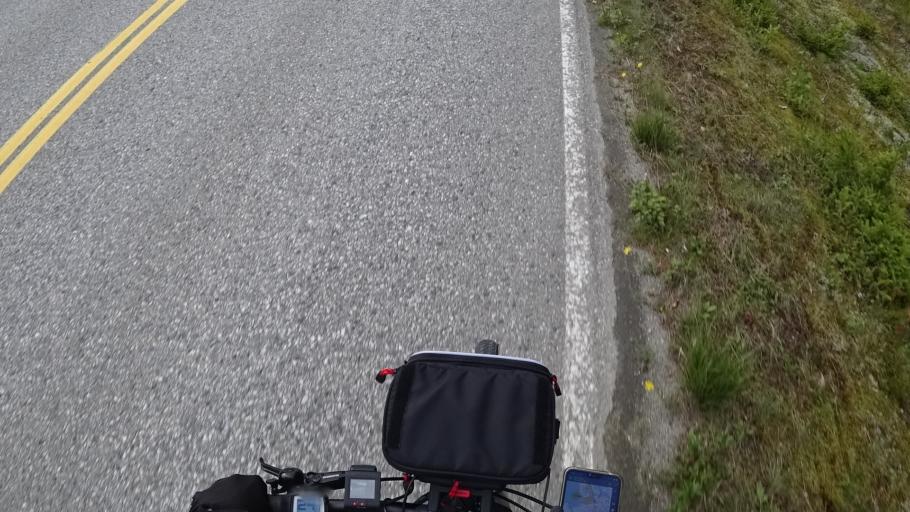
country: FI
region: North Karelia
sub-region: Joensuu
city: Ilomantsi
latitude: 62.6258
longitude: 31.2554
